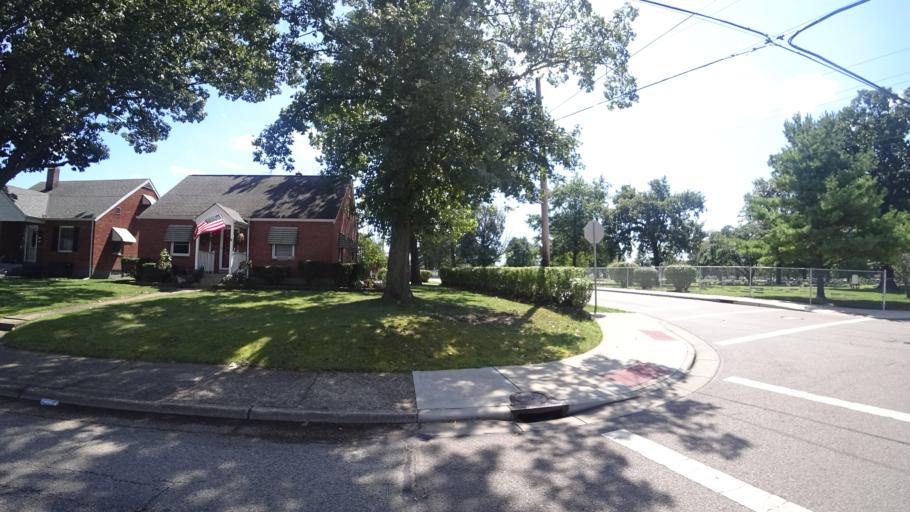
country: US
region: Ohio
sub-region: Butler County
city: Hamilton
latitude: 39.4056
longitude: -84.5375
